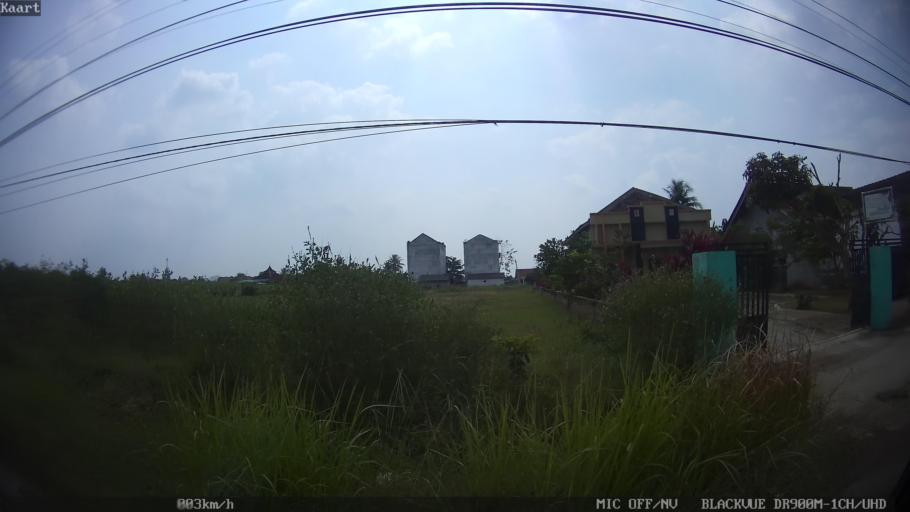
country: ID
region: Lampung
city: Gadingrejo
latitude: -5.3652
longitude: 105.0603
